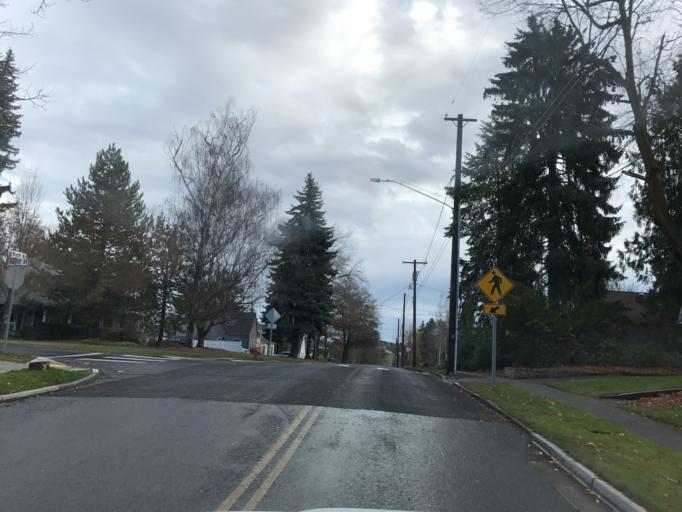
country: US
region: Idaho
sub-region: Latah County
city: Moscow
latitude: 46.7302
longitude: -116.9889
